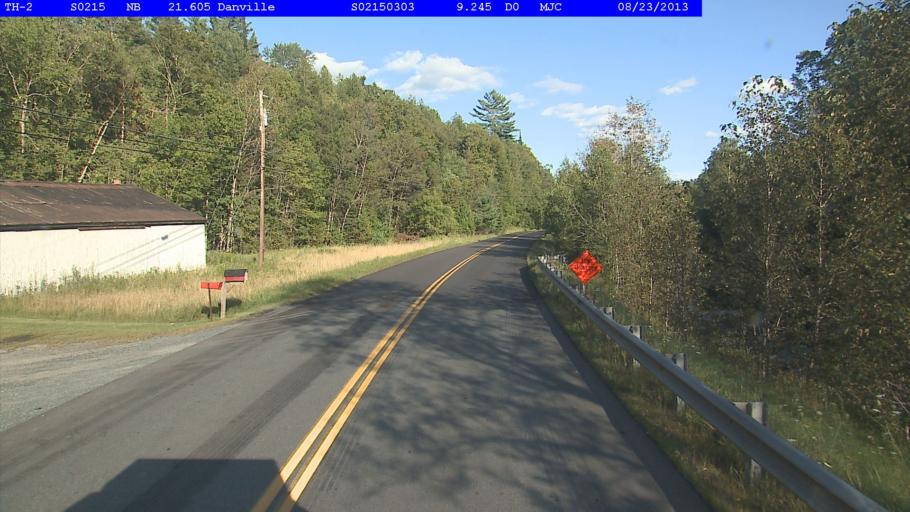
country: US
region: Vermont
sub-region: Caledonia County
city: St Johnsbury
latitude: 44.4555
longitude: -72.0786
